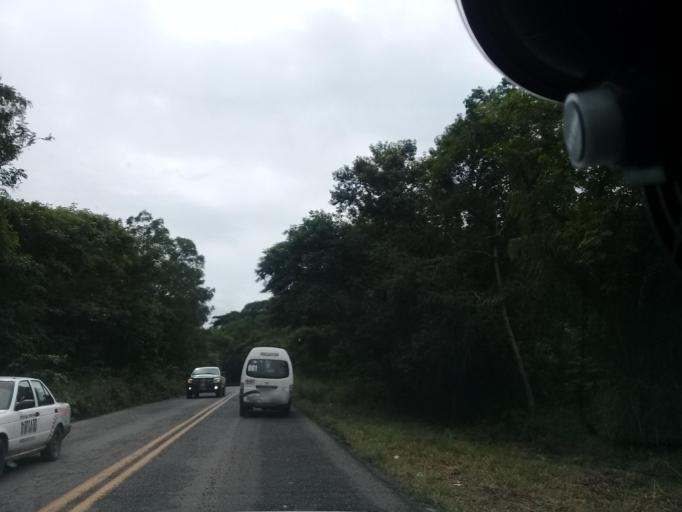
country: MX
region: Hidalgo
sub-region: Huejutla de Reyes
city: Parque de Poblamiento Solidaridad
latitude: 21.1957
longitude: -98.3920
